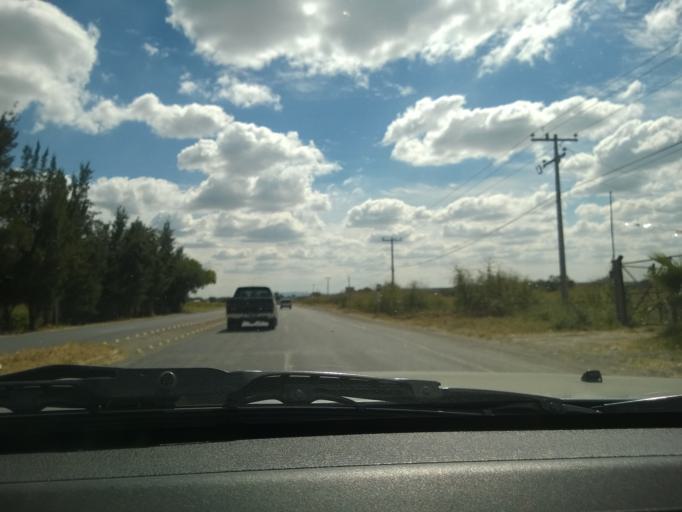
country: MX
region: Guanajuato
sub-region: Leon
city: El CERESO
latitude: 21.0177
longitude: -101.6991
